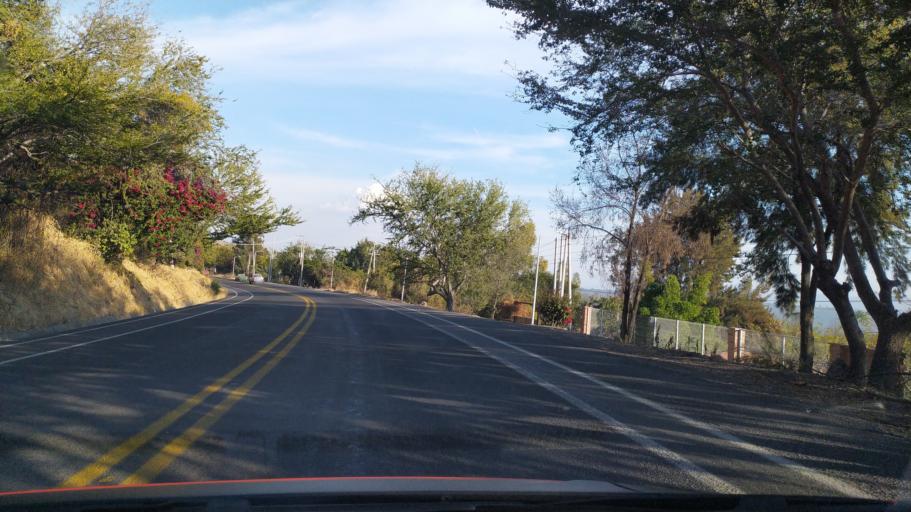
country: MX
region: Jalisco
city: Jamay
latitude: 20.2934
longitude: -102.7448
